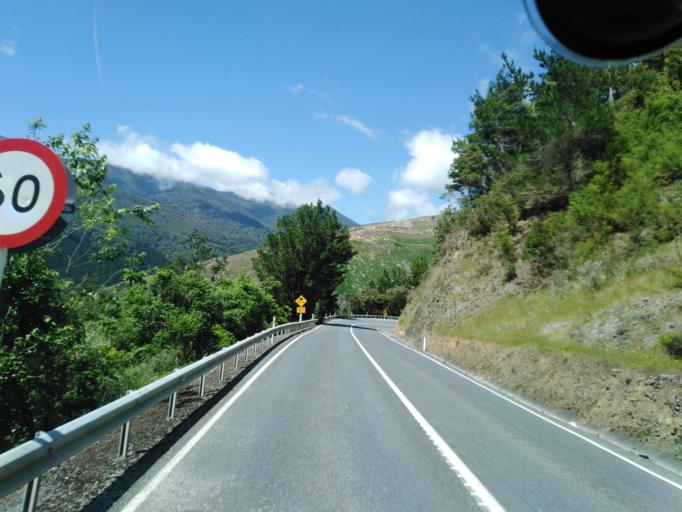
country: NZ
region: Nelson
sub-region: Nelson City
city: Nelson
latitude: -41.2282
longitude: 173.4242
